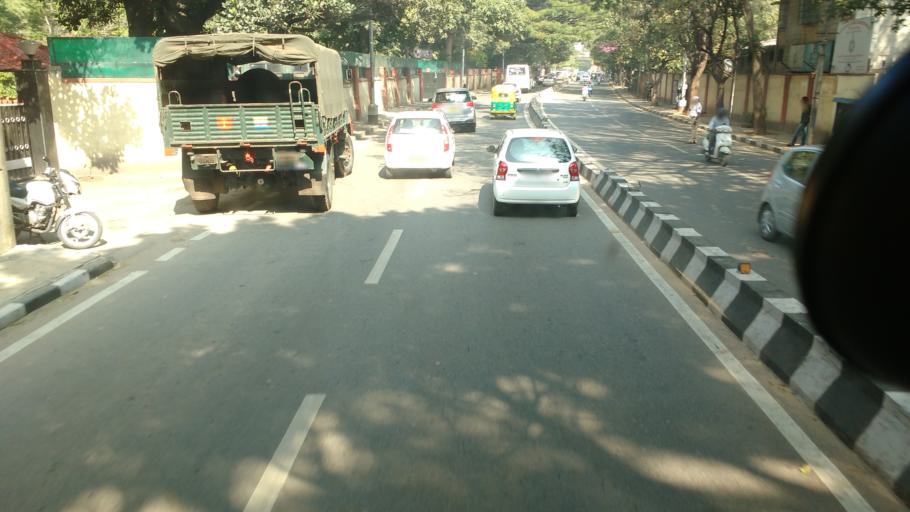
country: IN
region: Karnataka
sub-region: Bangalore Urban
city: Bangalore
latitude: 12.9681
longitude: 77.6200
